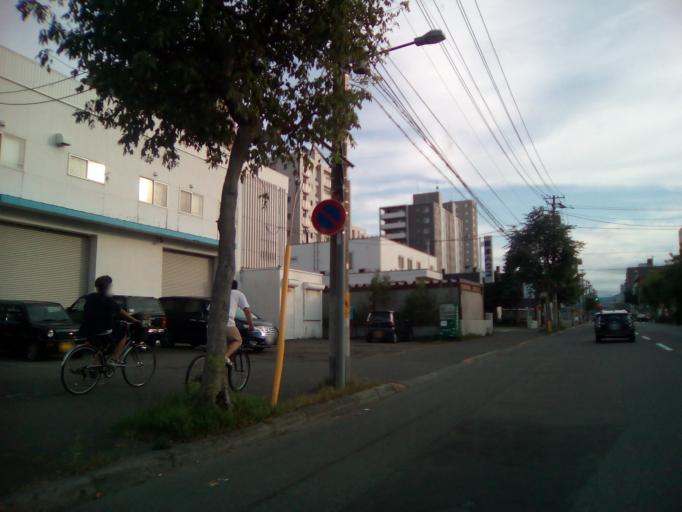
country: JP
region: Hokkaido
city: Sapporo
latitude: 43.0488
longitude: 141.3805
